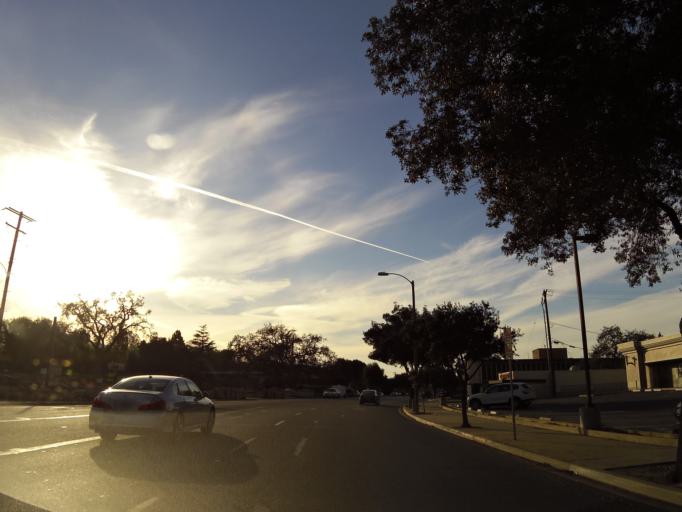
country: US
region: California
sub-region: Ventura County
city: Thousand Oaks
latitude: 34.1781
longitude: -118.8534
